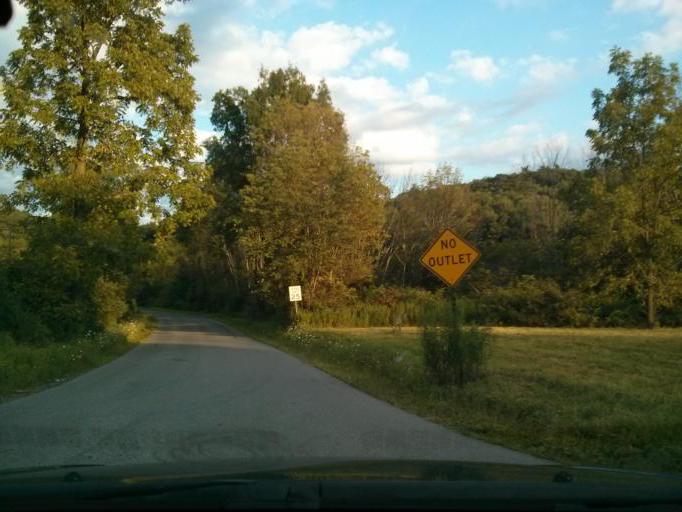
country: US
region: Pennsylvania
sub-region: Centre County
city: Park Forest Village
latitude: 40.8345
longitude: -77.9297
